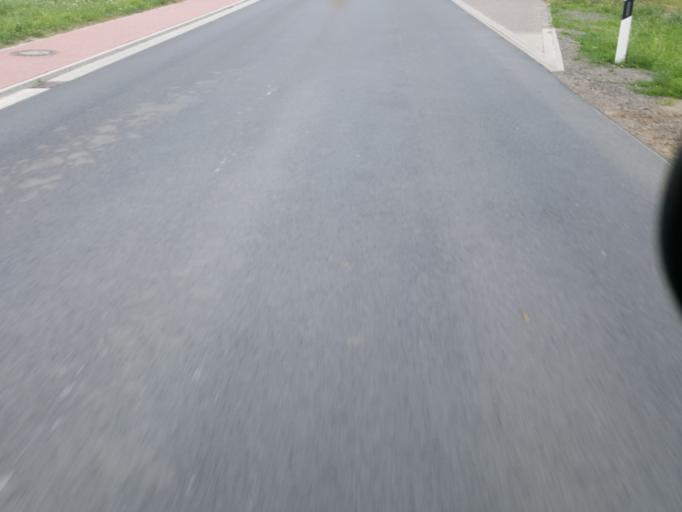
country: DE
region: Lower Saxony
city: Wolpinghausen
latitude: 52.4540
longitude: 9.2508
